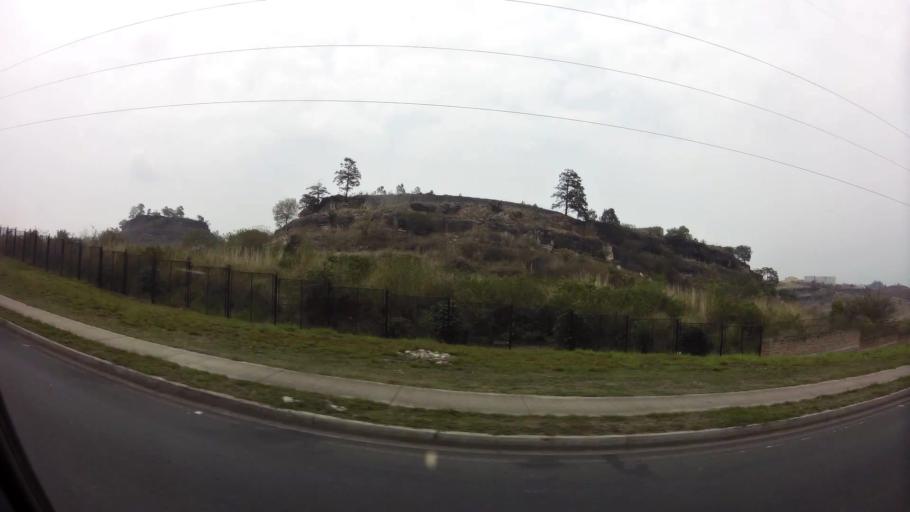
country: HN
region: Francisco Morazan
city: Yaguacire
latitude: 14.0463
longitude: -87.2512
